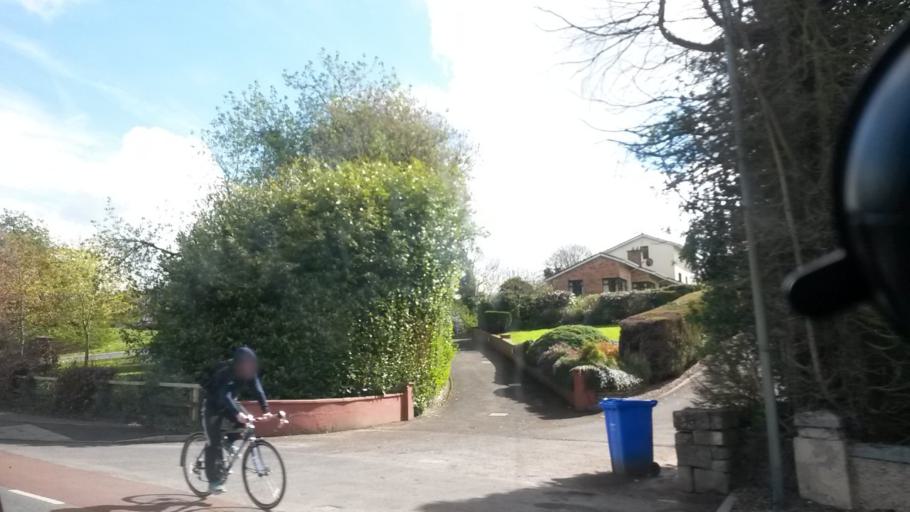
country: IE
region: Ulster
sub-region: An Cabhan
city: Cavan
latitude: 54.0042
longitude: -7.3503
